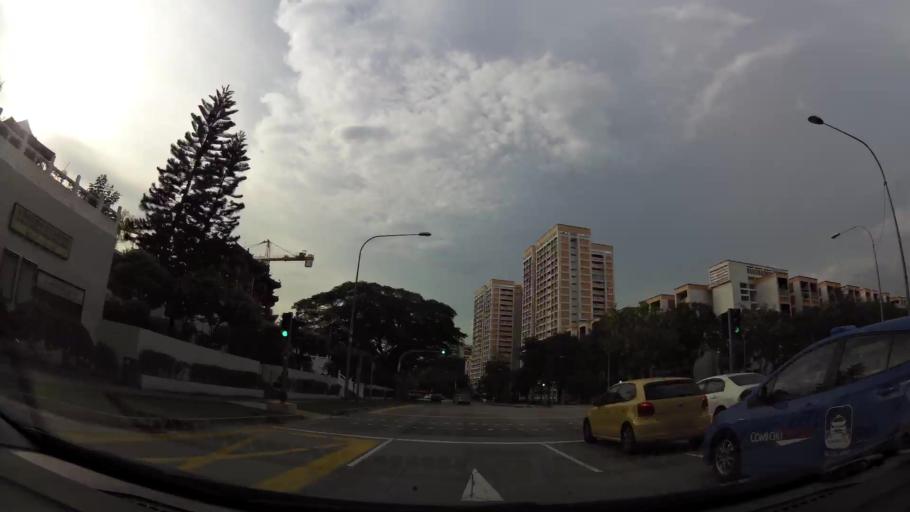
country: SG
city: Singapore
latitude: 1.3389
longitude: 103.8525
